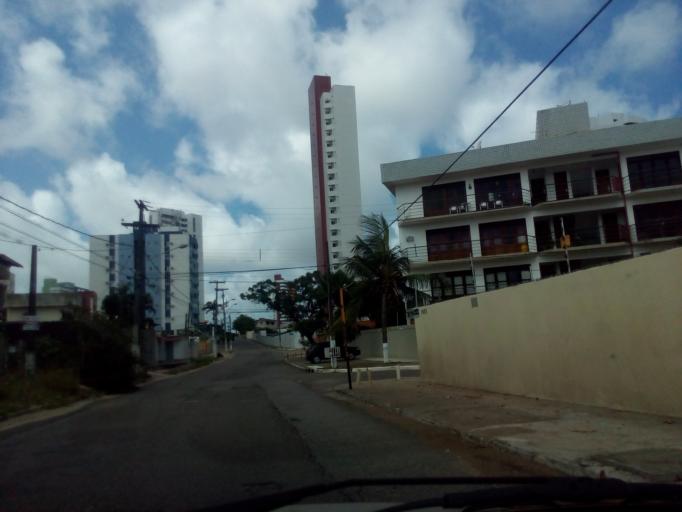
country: BR
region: Rio Grande do Norte
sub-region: Natal
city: Natal
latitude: -5.8582
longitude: -35.2047
